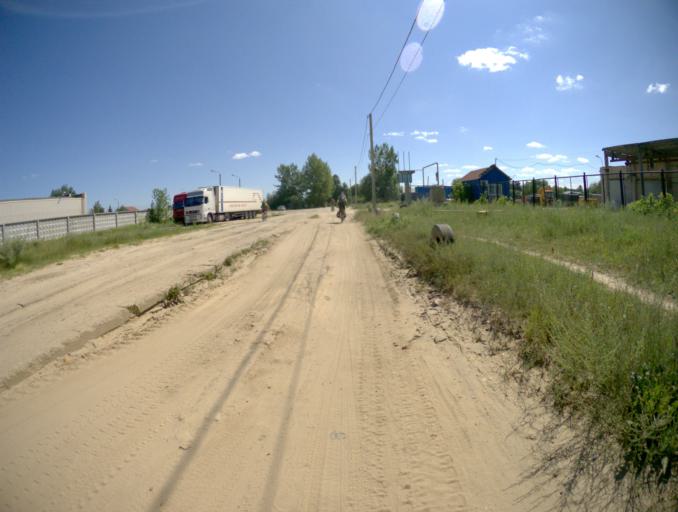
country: RU
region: Nizjnij Novgorod
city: Bor
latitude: 56.3728
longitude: 44.0530
